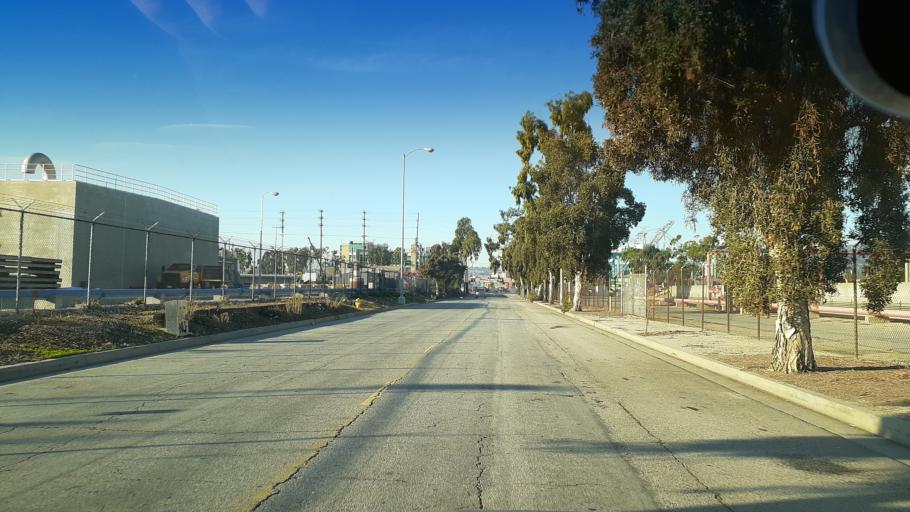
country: US
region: California
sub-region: Los Angeles County
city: San Pedro
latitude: 33.7446
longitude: -118.2639
